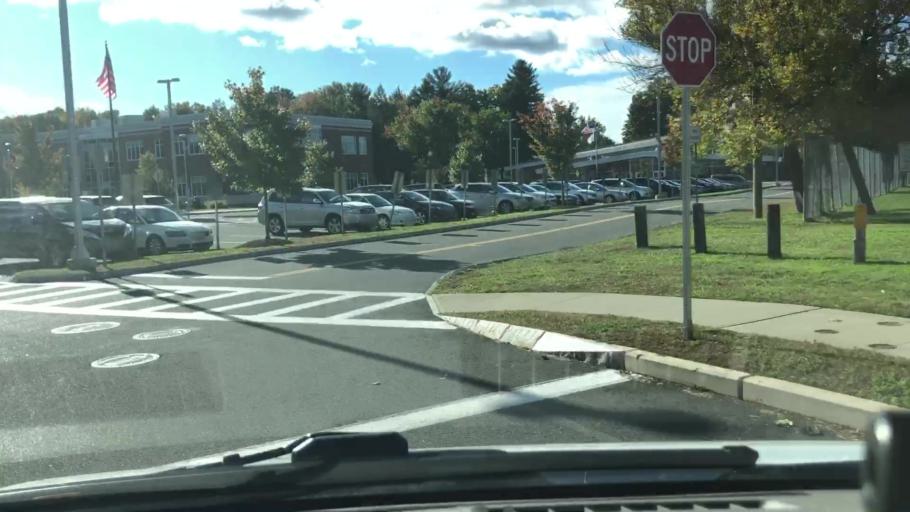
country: US
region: Massachusetts
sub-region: Franklin County
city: Greenfield
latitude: 42.6059
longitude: -72.5964
